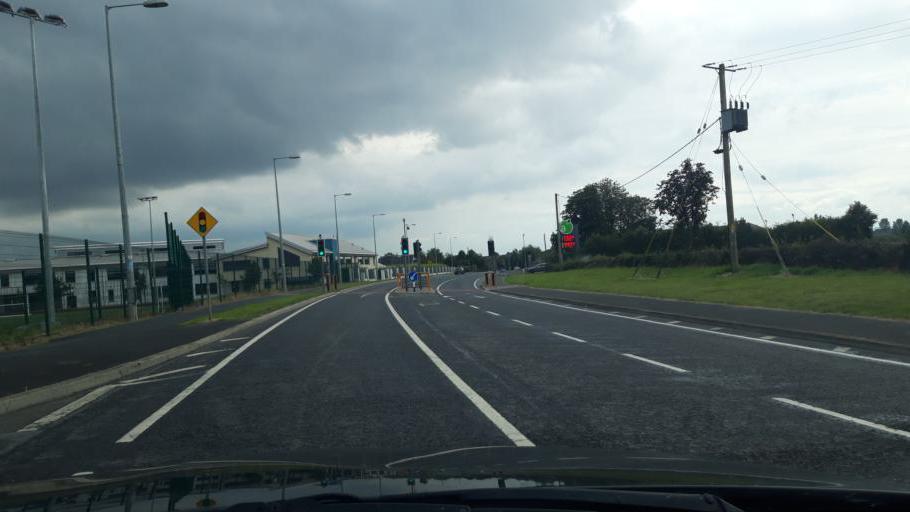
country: IE
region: Leinster
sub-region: Kildare
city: Athy
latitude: 53.0027
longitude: -6.9878
